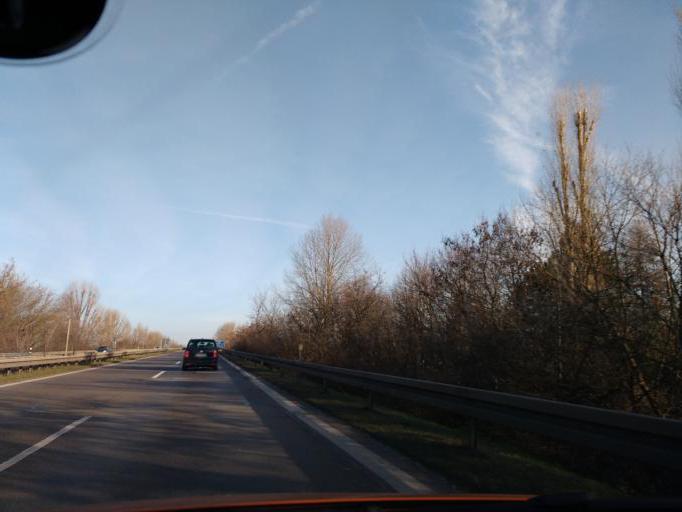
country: DE
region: Berlin
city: Heinersdorf
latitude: 52.5865
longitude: 13.4350
